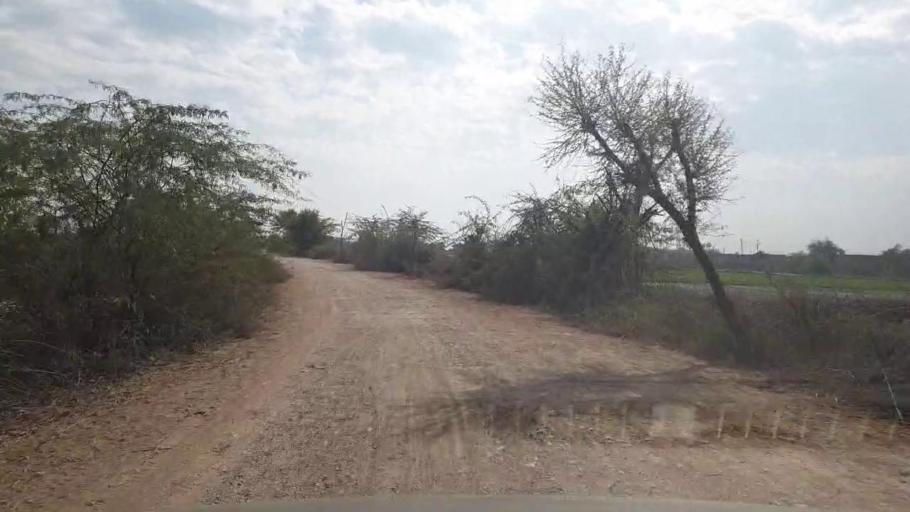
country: PK
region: Sindh
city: Sakrand
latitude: 26.0045
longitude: 68.4047
